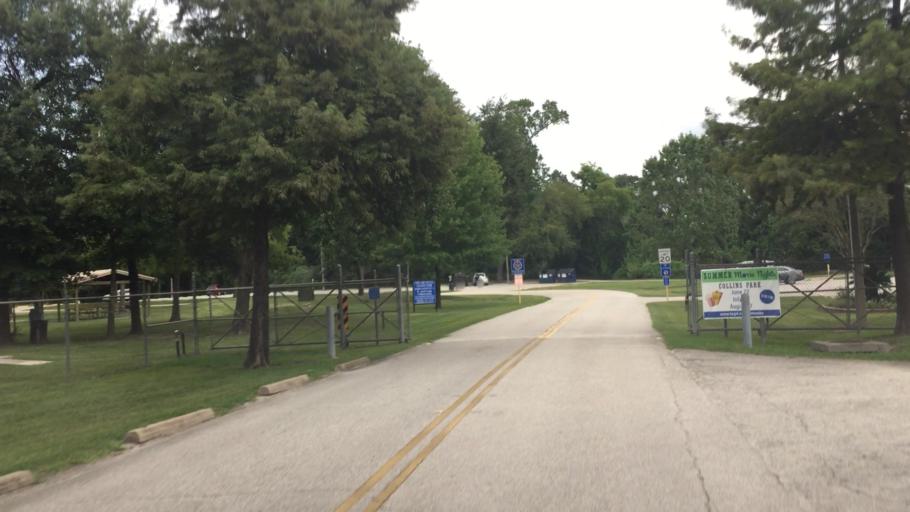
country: US
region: Texas
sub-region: Harris County
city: Hudson
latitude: 30.0109
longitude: -95.5104
